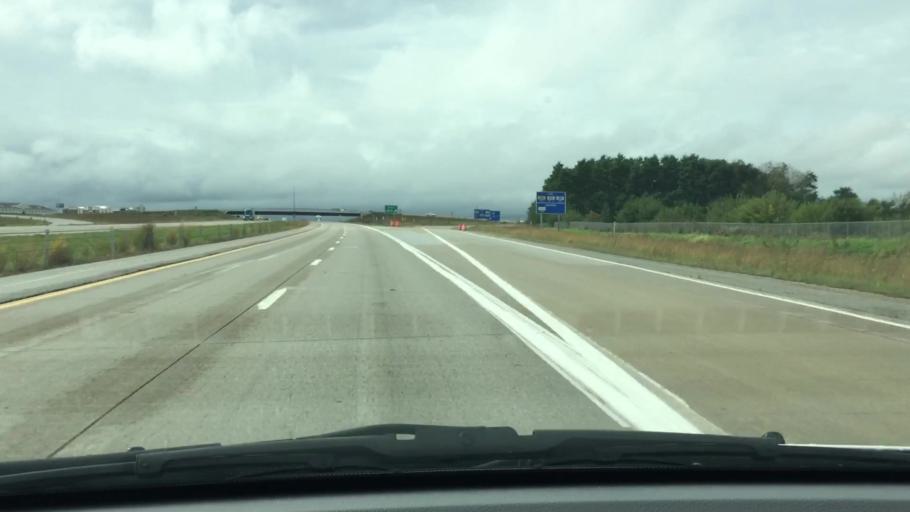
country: US
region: Iowa
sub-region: Polk County
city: Altoona
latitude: 41.6695
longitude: -93.4581
